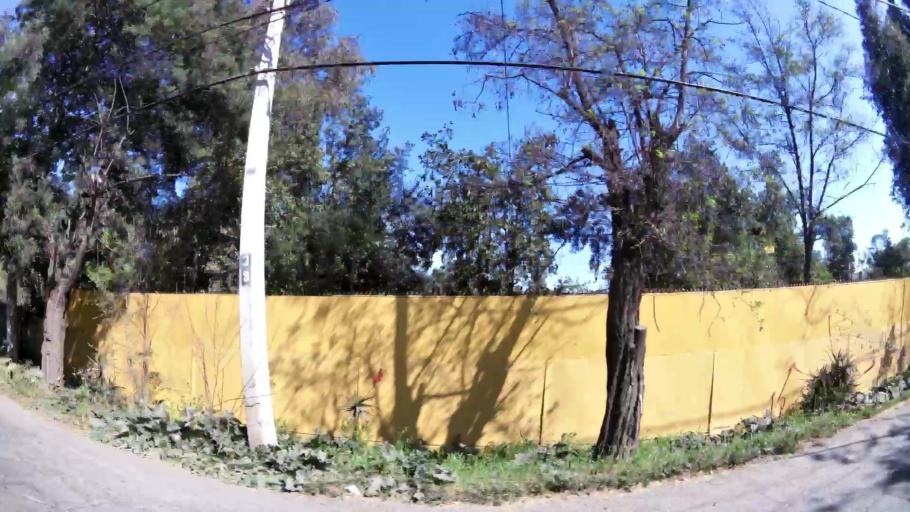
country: CL
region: Santiago Metropolitan
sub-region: Provincia de Santiago
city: Villa Presidente Frei, Nunoa, Santiago, Chile
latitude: -33.4411
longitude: -70.5186
